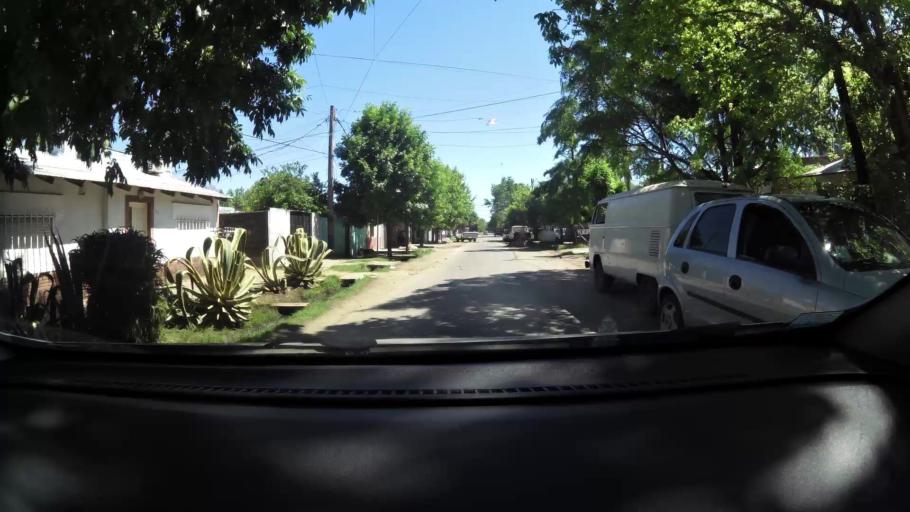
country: AR
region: Santa Fe
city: Perez
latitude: -32.9681
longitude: -60.7069
